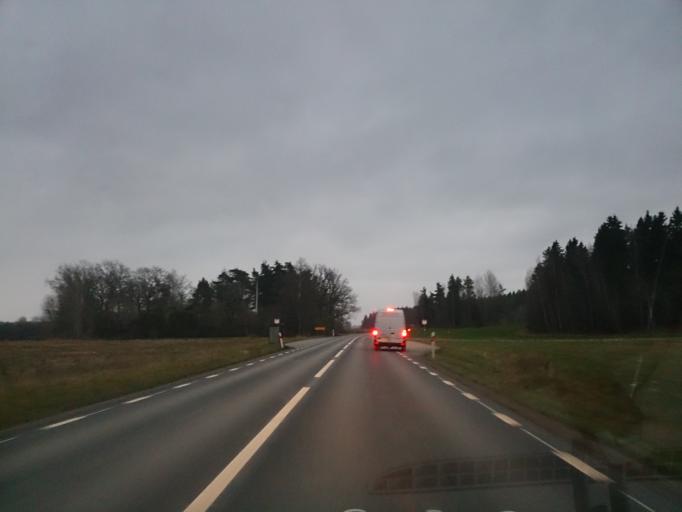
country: SE
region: OEstergoetland
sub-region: Linkopings Kommun
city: Linghem
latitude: 58.3694
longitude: 15.8182
